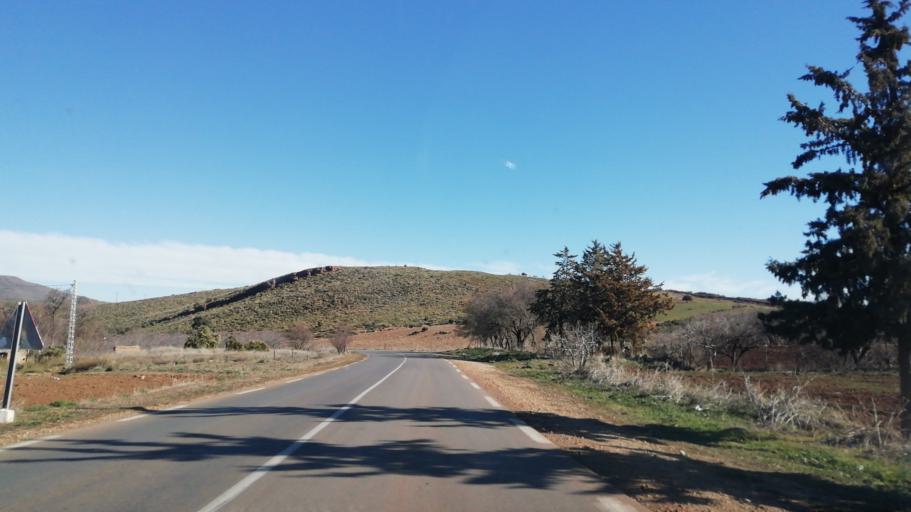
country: DZ
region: Tlemcen
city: Ouled Mimoun
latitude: 34.7654
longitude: -1.1385
